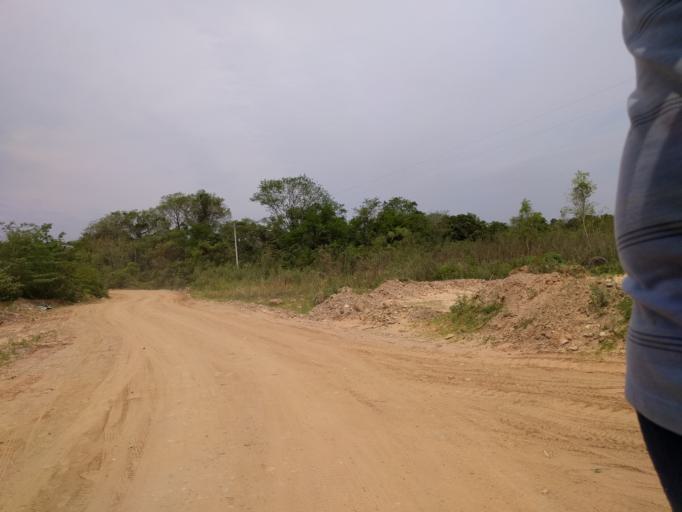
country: BO
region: Santa Cruz
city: Santa Rita
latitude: -17.9389
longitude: -63.3635
